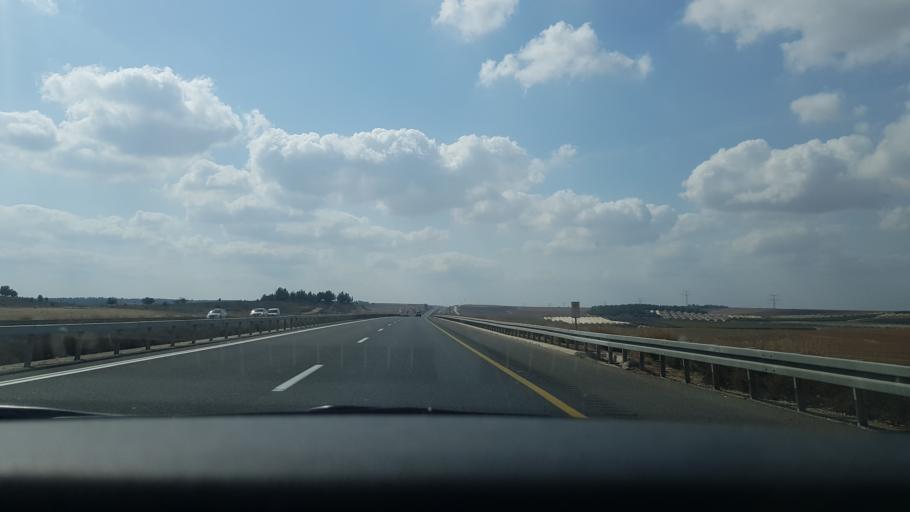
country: IL
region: Southern District
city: Qiryat Gat
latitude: 31.5696
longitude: 34.8052
